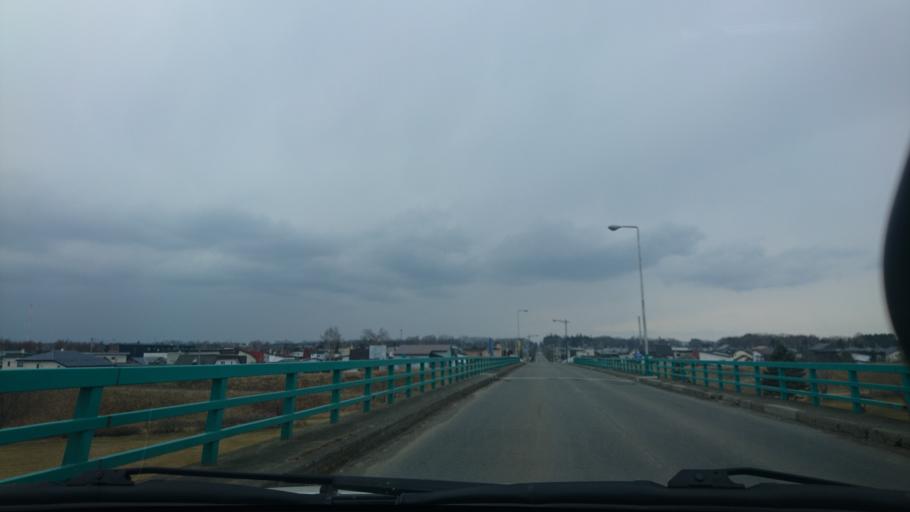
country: JP
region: Hokkaido
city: Otofuke
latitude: 42.9928
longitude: 143.2126
